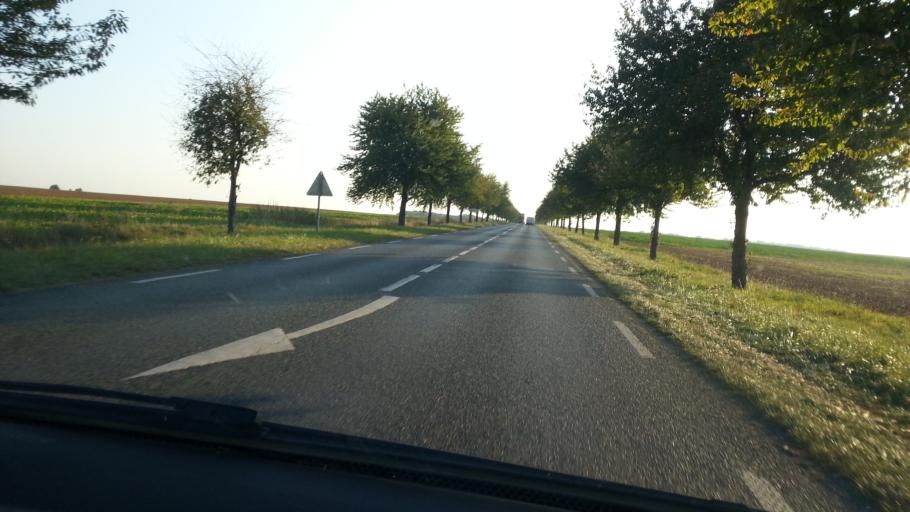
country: FR
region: Picardie
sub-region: Departement de l'Oise
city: Estrees-Saint-Denis
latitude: 49.4204
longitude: 2.6346
